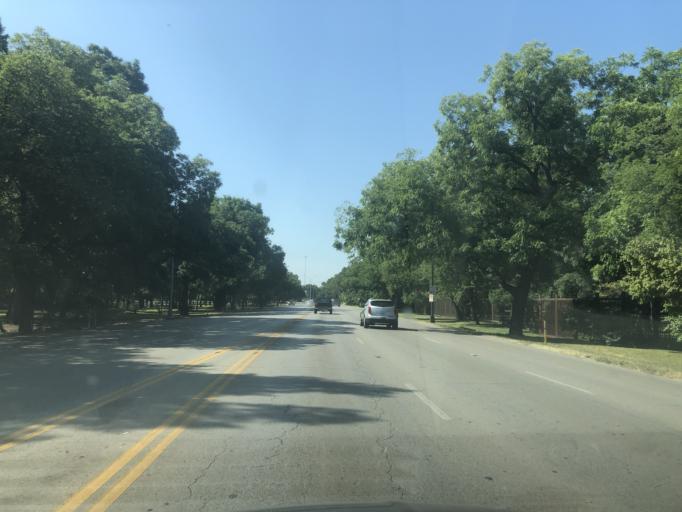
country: US
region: Texas
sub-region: Tarrant County
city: Fort Worth
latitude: 32.7396
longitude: -97.3615
